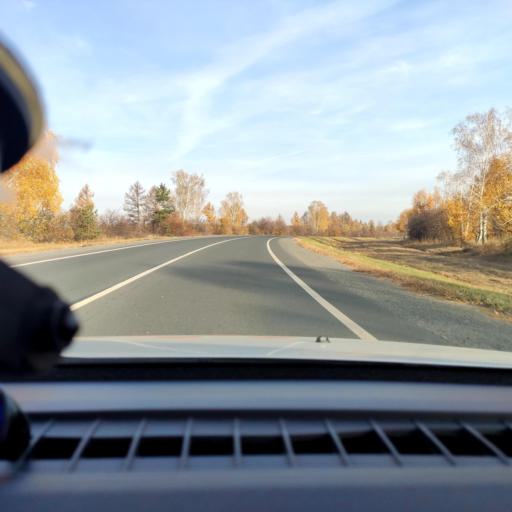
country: RU
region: Samara
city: Volzhskiy
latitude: 53.4766
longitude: 50.1170
